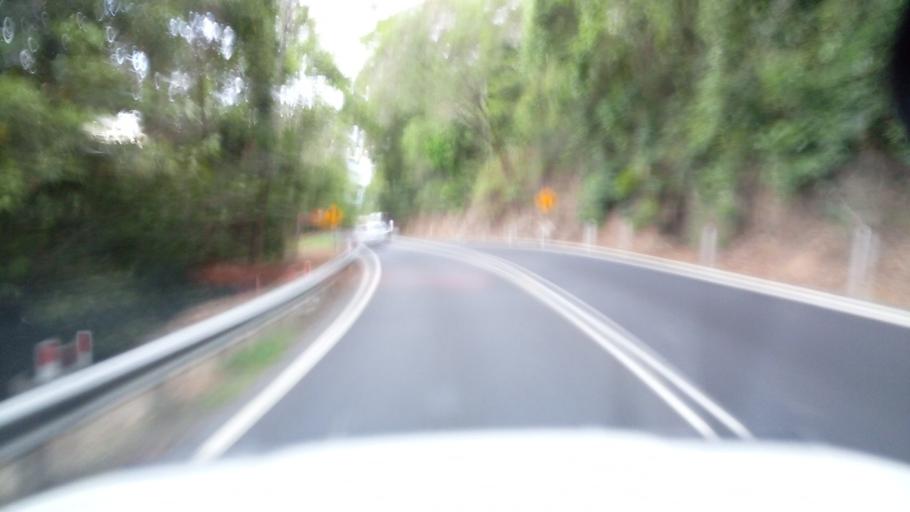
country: AU
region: Queensland
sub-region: Tablelands
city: Kuranda
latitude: -16.8347
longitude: 145.6708
